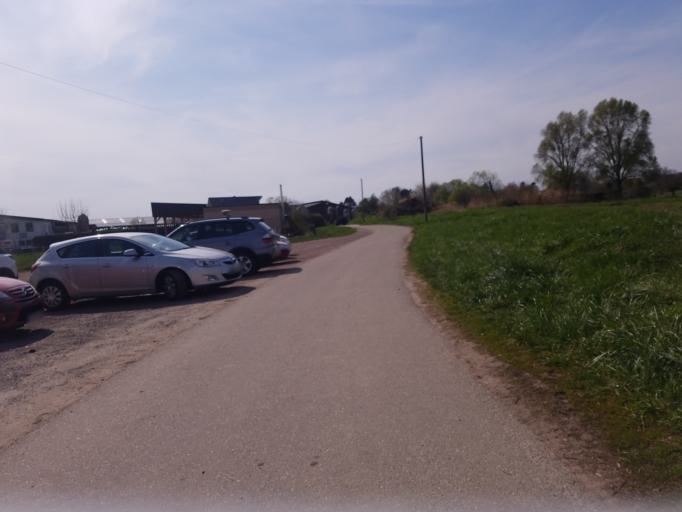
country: FR
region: Alsace
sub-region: Departement du Bas-Rhin
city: Soufflenheim
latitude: 48.8979
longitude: 7.9873
